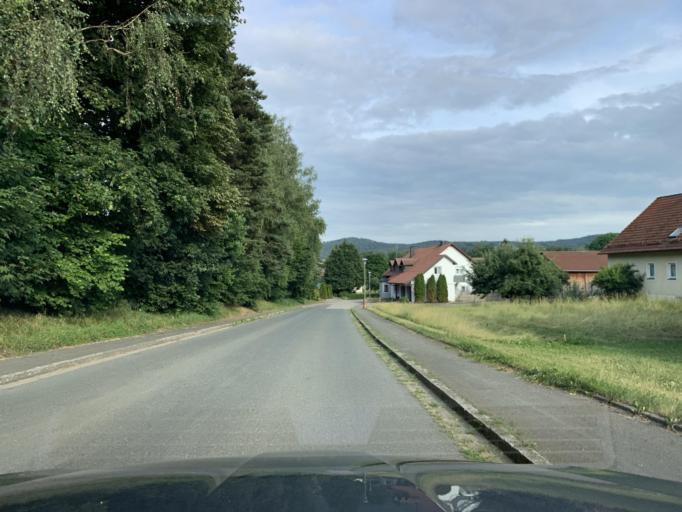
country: DE
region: Bavaria
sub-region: Upper Palatinate
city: Bach
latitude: 49.4039
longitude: 12.3886
